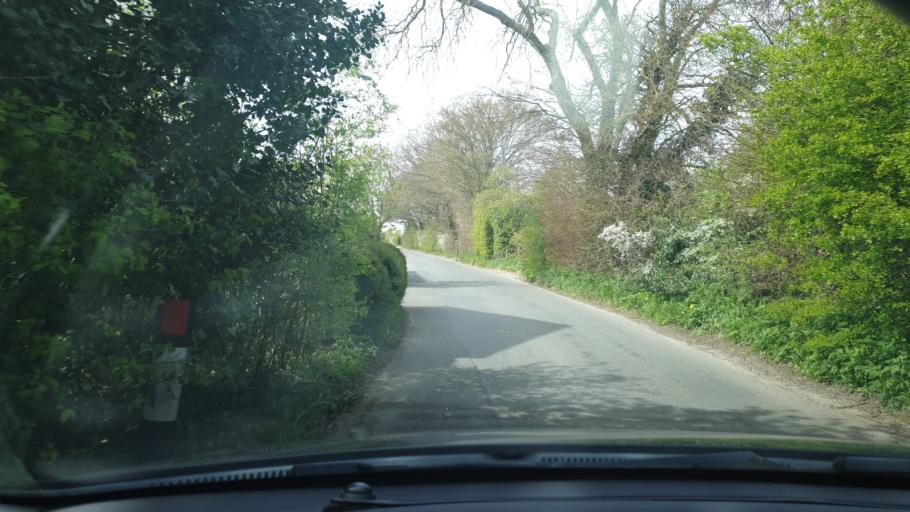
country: GB
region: England
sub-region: Essex
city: Mistley
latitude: 51.9014
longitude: 1.1350
